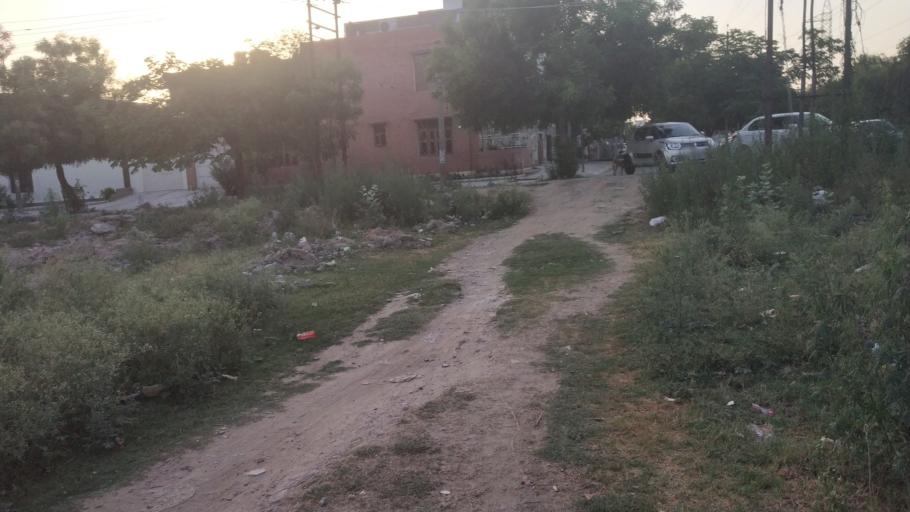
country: IN
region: Punjab
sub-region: Ajitgarh
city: Mohali
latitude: 30.6856
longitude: 76.7308
